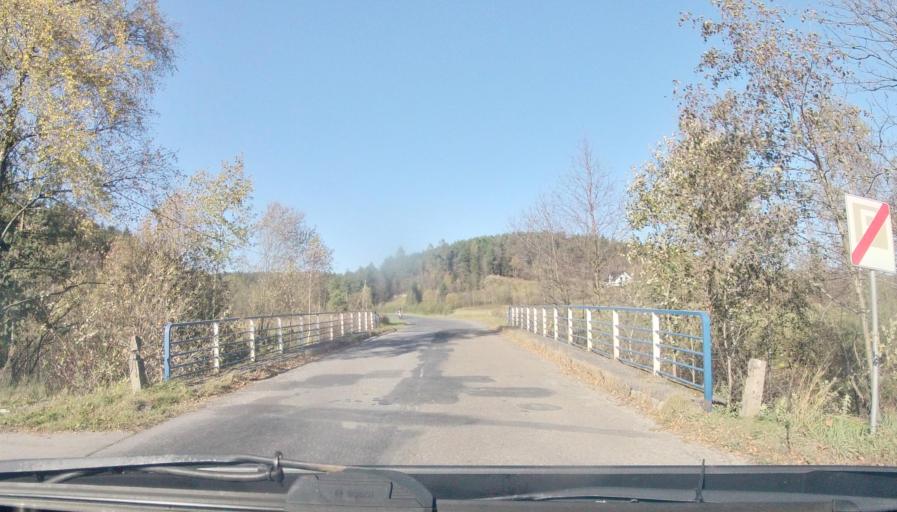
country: PL
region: Lesser Poland Voivodeship
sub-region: Powiat suski
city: Kukow
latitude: 49.7492
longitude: 19.4647
